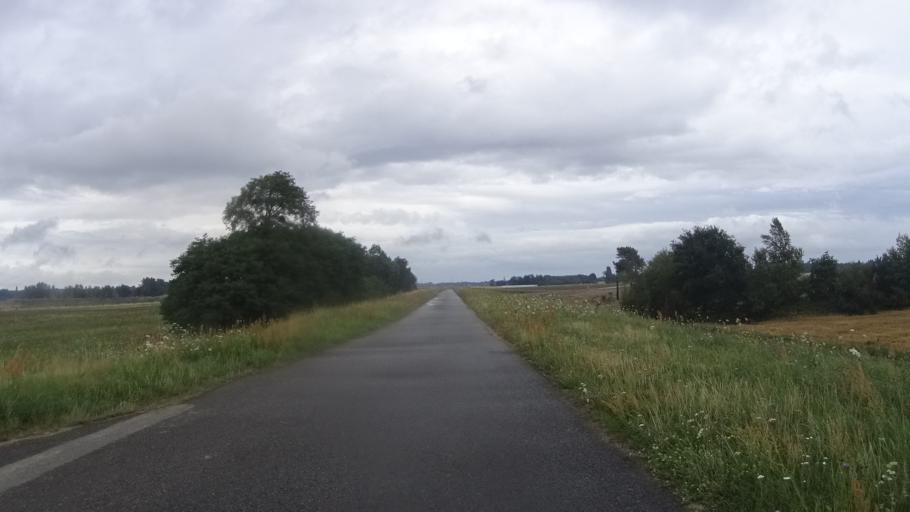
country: FR
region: Centre
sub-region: Departement du Loiret
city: Mardie
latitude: 47.8560
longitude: 2.0627
